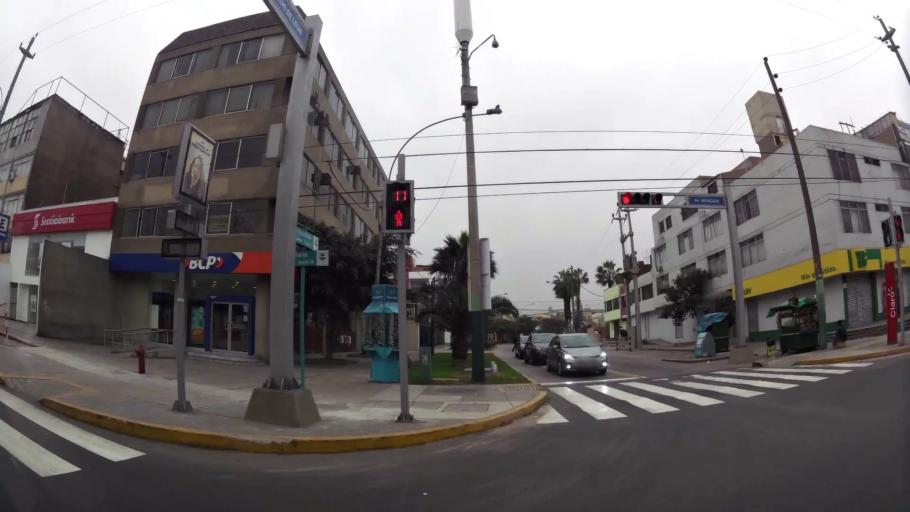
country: PE
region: Lima
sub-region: Lima
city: San Luis
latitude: -12.0979
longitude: -77.0021
